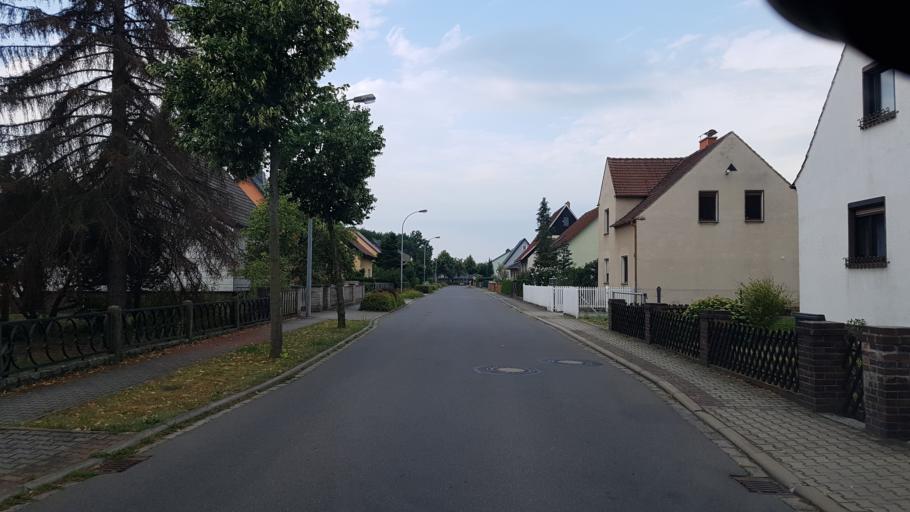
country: DE
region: Brandenburg
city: Tettau
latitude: 51.4260
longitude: 13.7280
